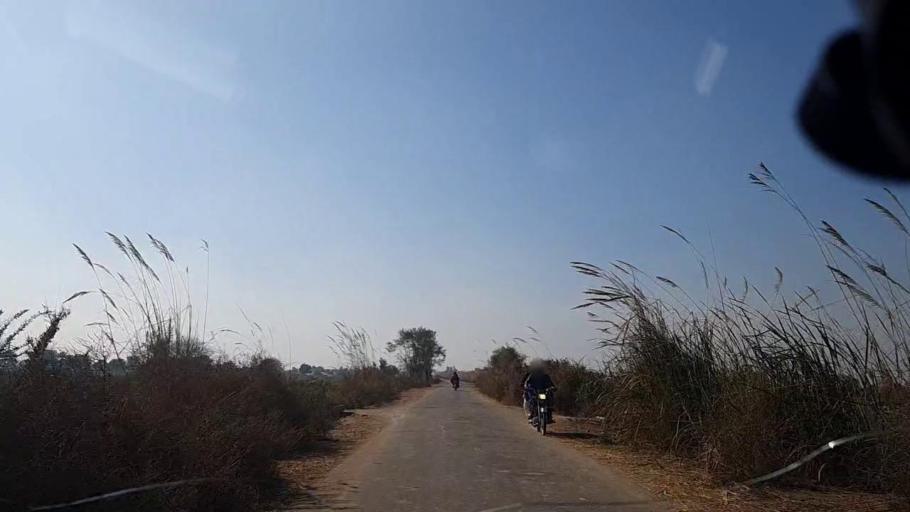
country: PK
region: Sindh
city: Khanpur
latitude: 27.7301
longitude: 69.4479
